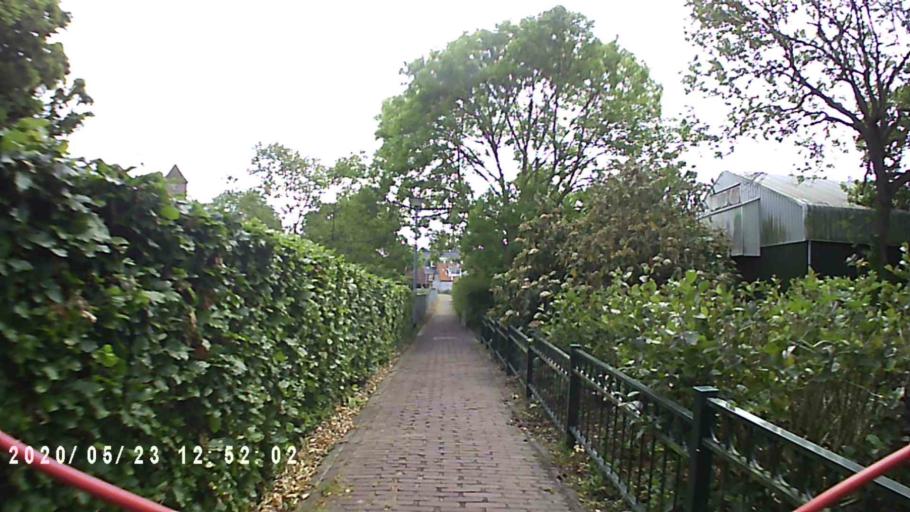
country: NL
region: Groningen
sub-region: Gemeente Delfzijl
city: Delfzijl
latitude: 53.2985
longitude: 7.0443
